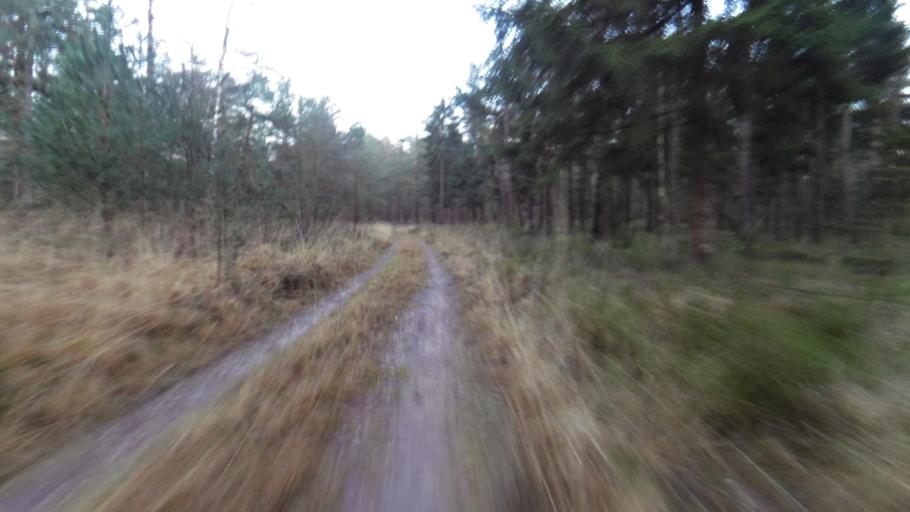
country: NL
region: Gelderland
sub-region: Gemeente Apeldoorn
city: Uddel
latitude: 52.2803
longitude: 5.8578
